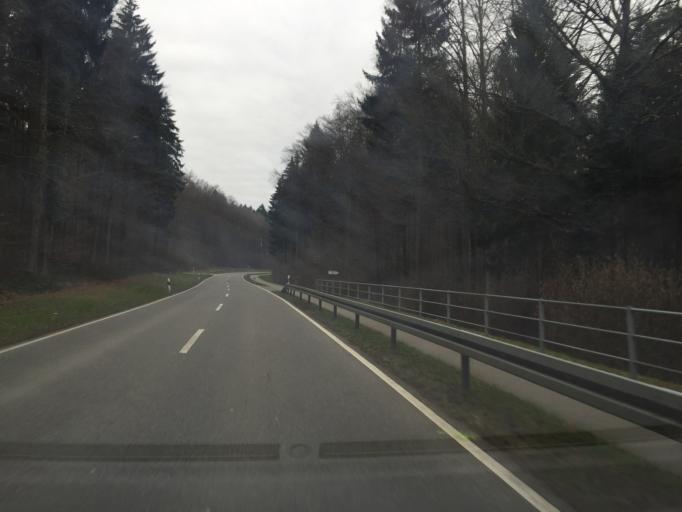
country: DE
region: Baden-Wuerttemberg
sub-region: Freiburg Region
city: Gailingen
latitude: 47.7100
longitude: 8.7469
